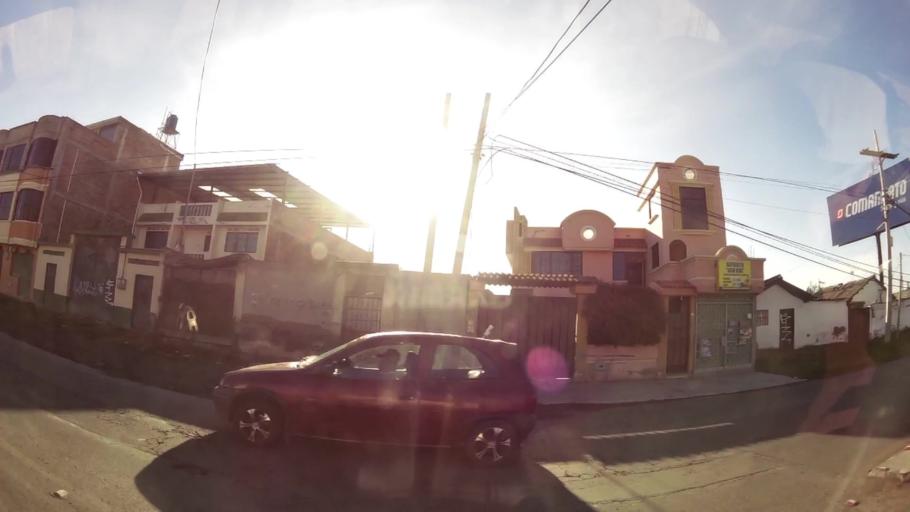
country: EC
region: Chimborazo
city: Riobamba
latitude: -1.6492
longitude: -78.6426
